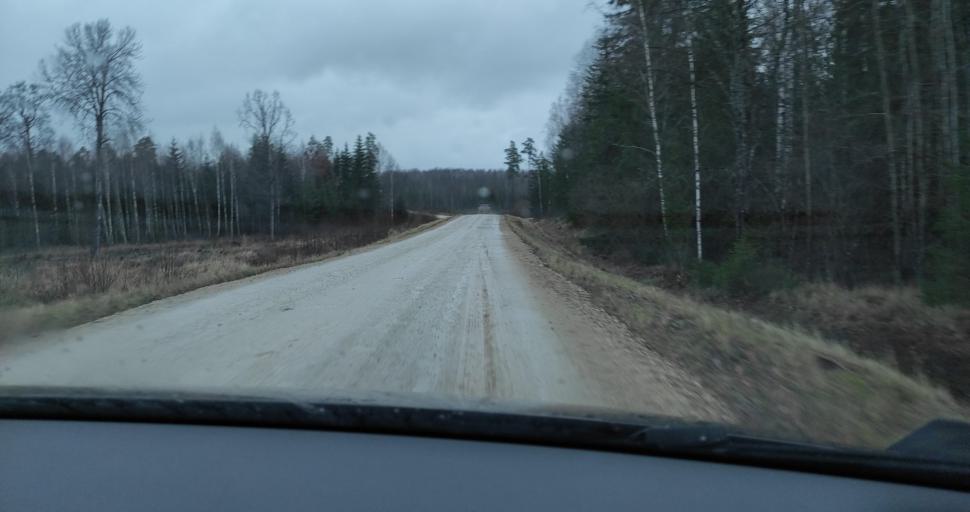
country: LV
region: Skrunda
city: Skrunda
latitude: 56.5643
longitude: 22.1320
